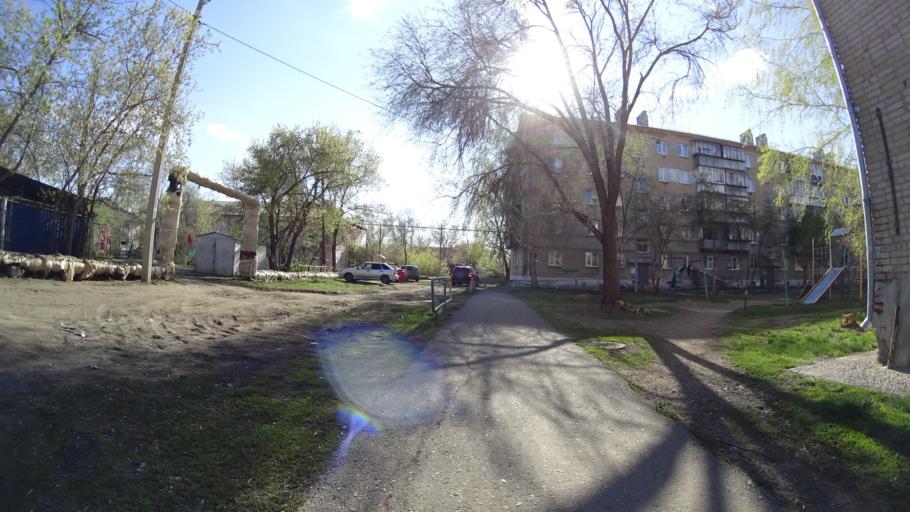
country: RU
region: Chelyabinsk
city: Troitsk
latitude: 54.1044
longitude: 61.5585
